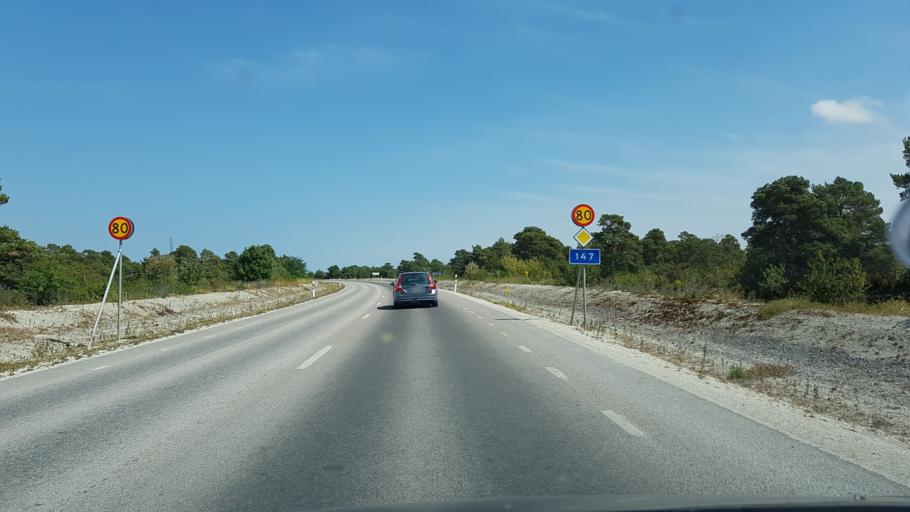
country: SE
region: Gotland
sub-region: Gotland
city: Visby
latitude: 57.6301
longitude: 18.3461
